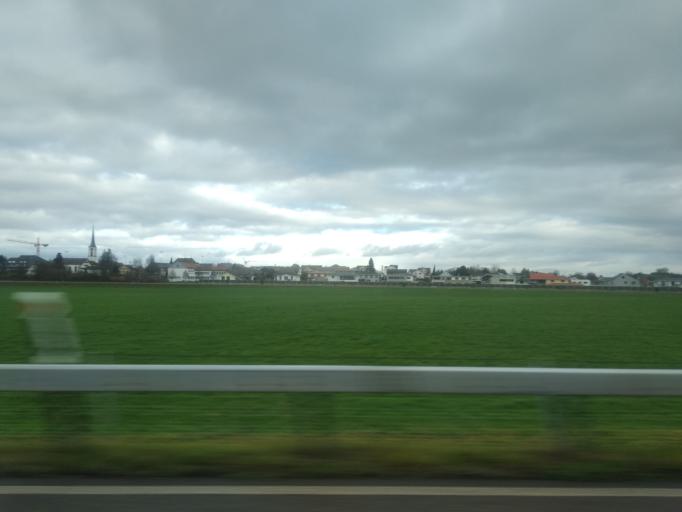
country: CH
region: Saint Gallen
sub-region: Wahlkreis Wil
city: Flawil
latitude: 47.4337
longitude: 9.1999
